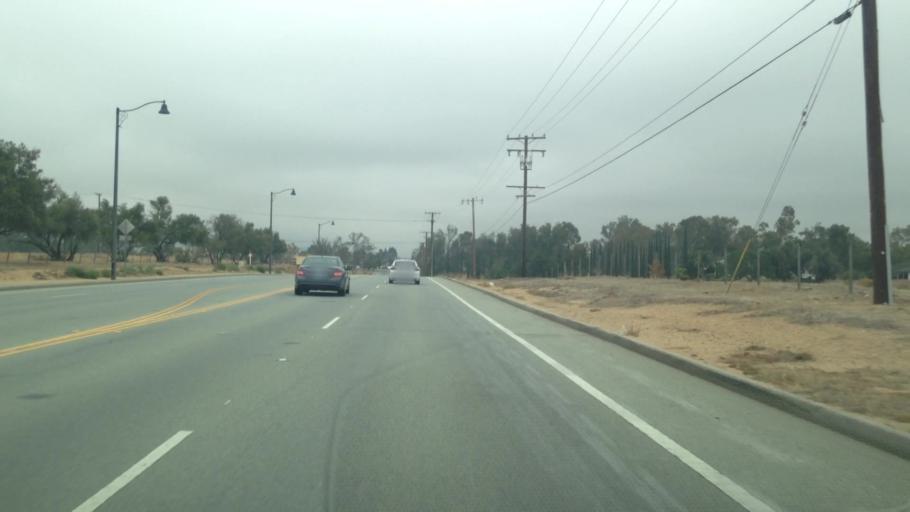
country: US
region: California
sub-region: Riverside County
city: Beaumont
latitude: 33.9470
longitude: -116.9840
